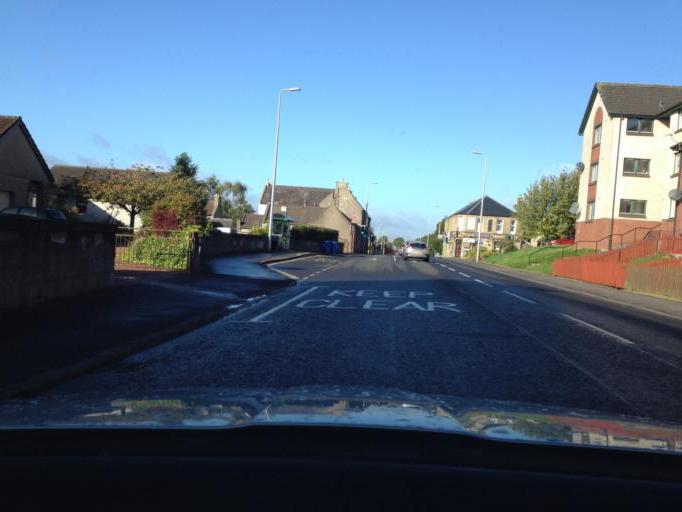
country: GB
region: Scotland
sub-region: West Lothian
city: Blackburn
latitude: 55.8711
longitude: -3.6214
